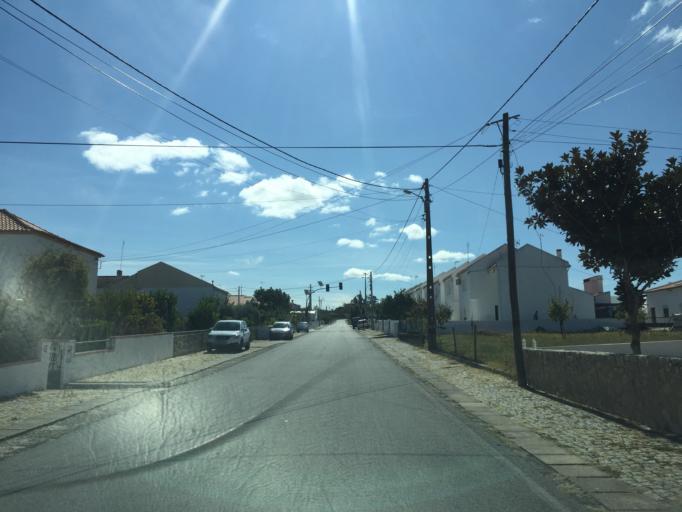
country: PT
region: Portalegre
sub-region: Marvao
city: Marvao
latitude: 39.4456
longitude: -7.3699
